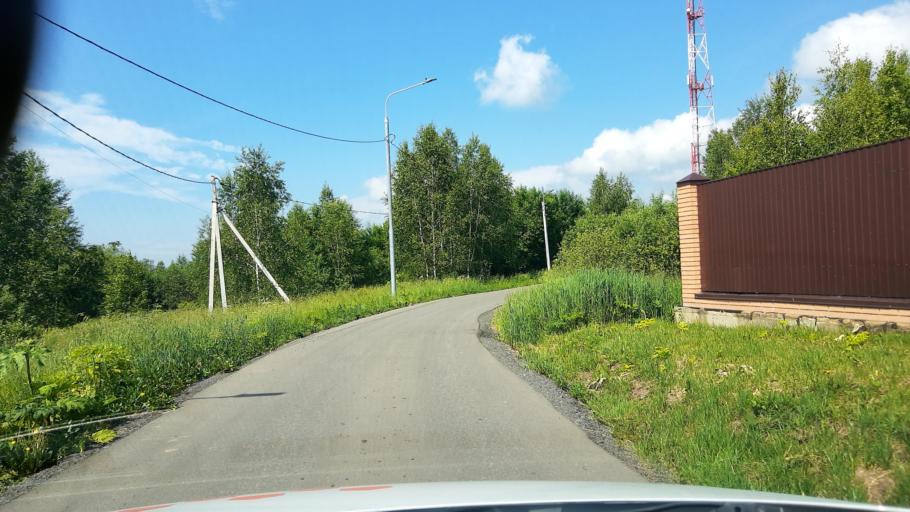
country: RU
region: Moskovskaya
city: Kievskij
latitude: 55.2236
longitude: 36.9821
